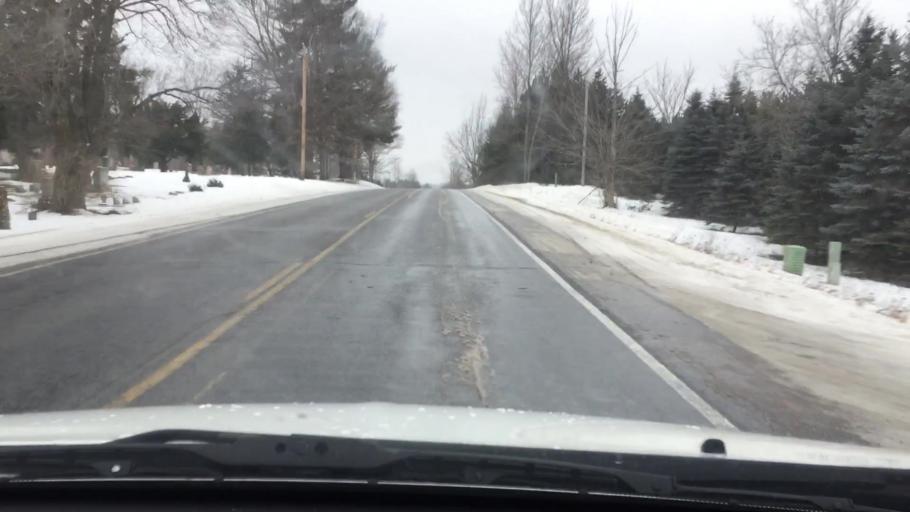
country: US
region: Michigan
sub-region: Wexford County
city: Cadillac
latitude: 44.0675
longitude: -85.4440
